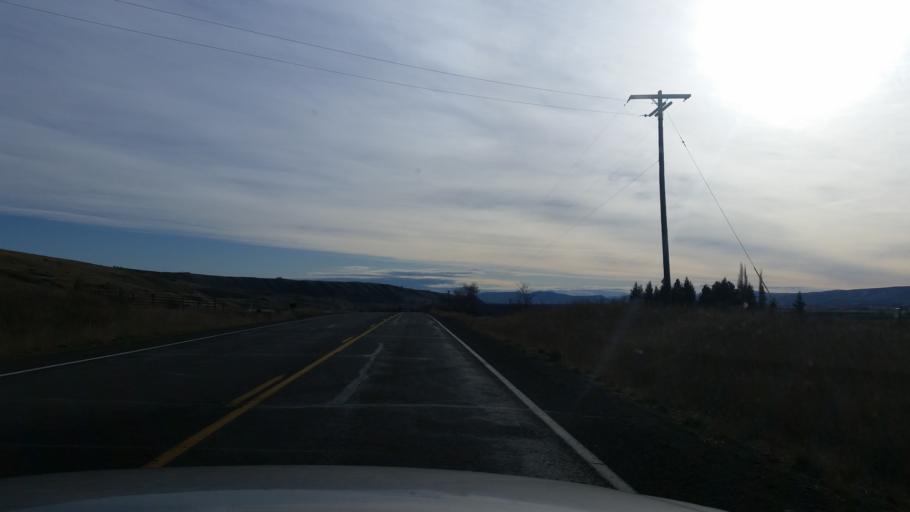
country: US
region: Washington
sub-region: Kittitas County
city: Ellensburg
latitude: 47.1060
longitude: -120.7096
